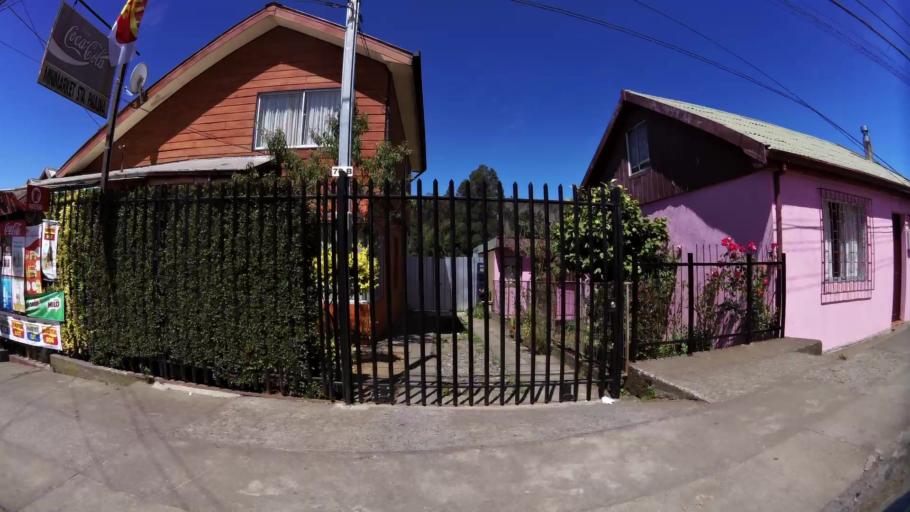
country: CL
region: Biobio
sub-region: Provincia de Concepcion
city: Penco
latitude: -36.7480
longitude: -72.9939
